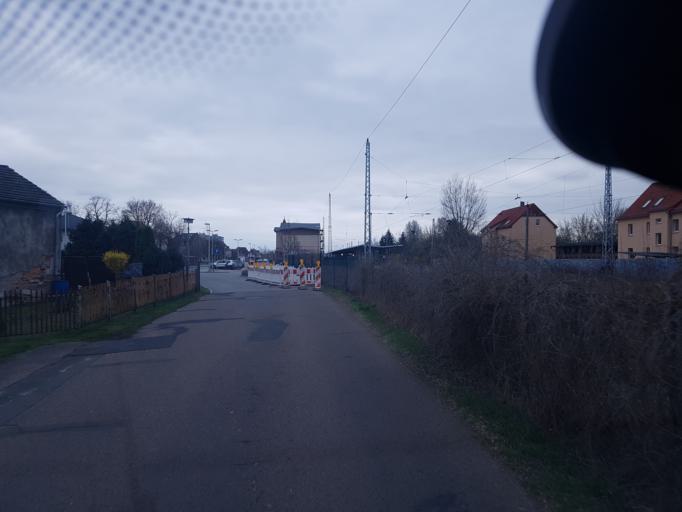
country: DE
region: Brandenburg
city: Eisenhuettenstadt
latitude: 52.1498
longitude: 14.6589
